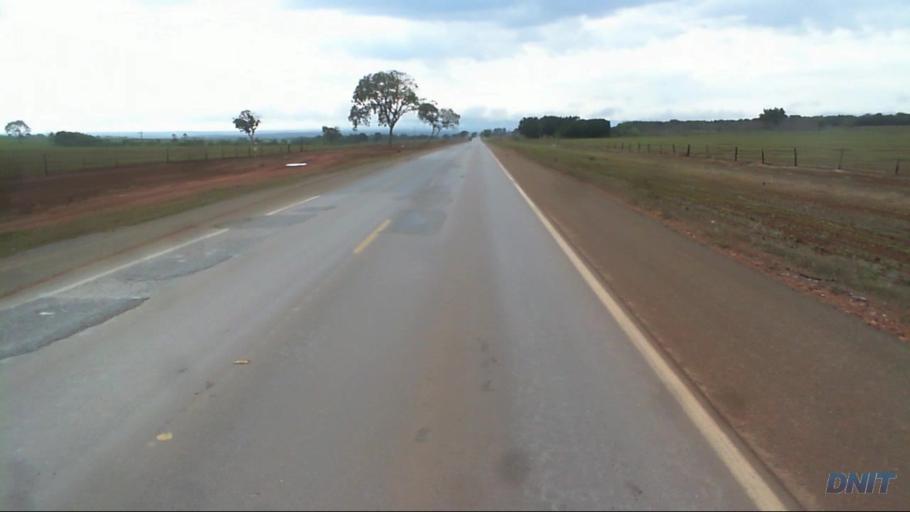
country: BR
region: Goias
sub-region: Uruacu
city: Uruacu
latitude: -14.6987
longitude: -49.1200
